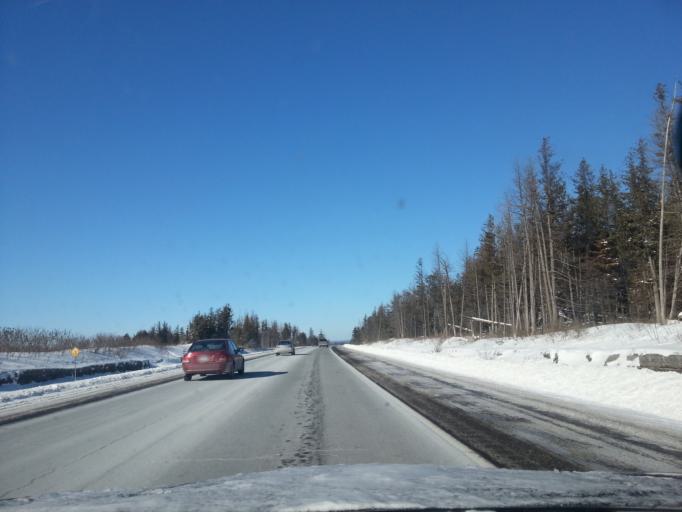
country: CA
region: Ontario
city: Arnprior
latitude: 45.3401
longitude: -76.1888
